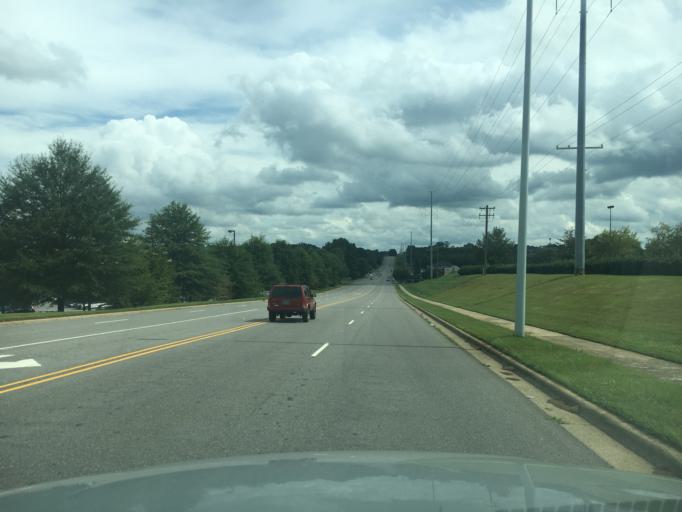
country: US
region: North Carolina
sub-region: Catawba County
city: Hickory
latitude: 35.7023
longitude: -81.3077
